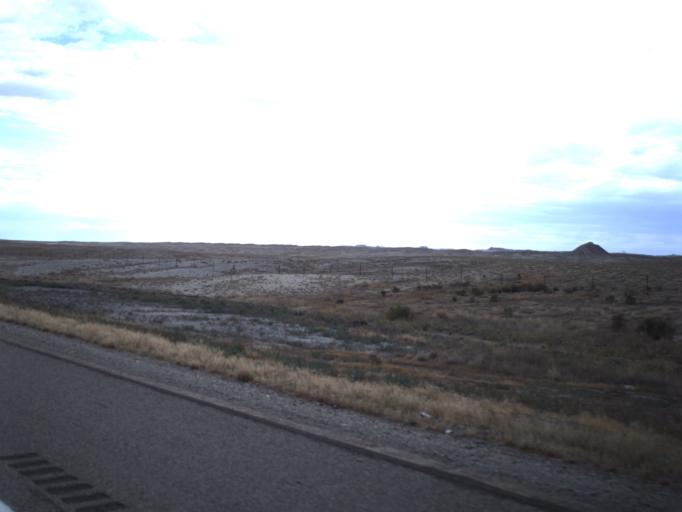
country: US
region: Utah
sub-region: Grand County
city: Moab
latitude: 38.9367
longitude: -110.0285
